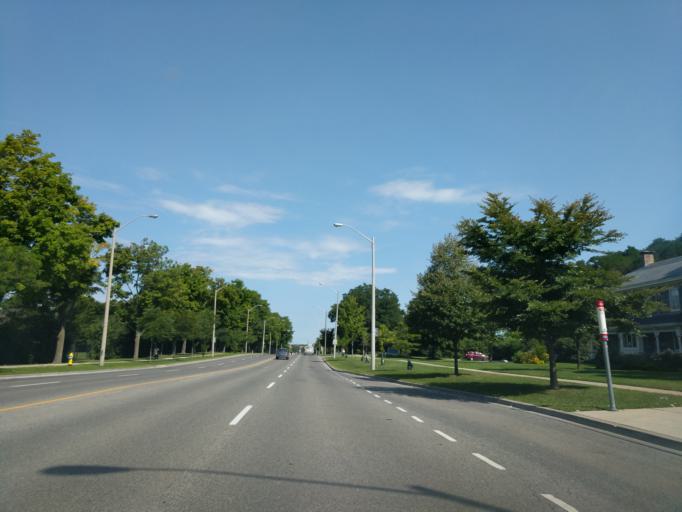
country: CA
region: Ontario
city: Scarborough
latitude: 43.8126
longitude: -79.2258
